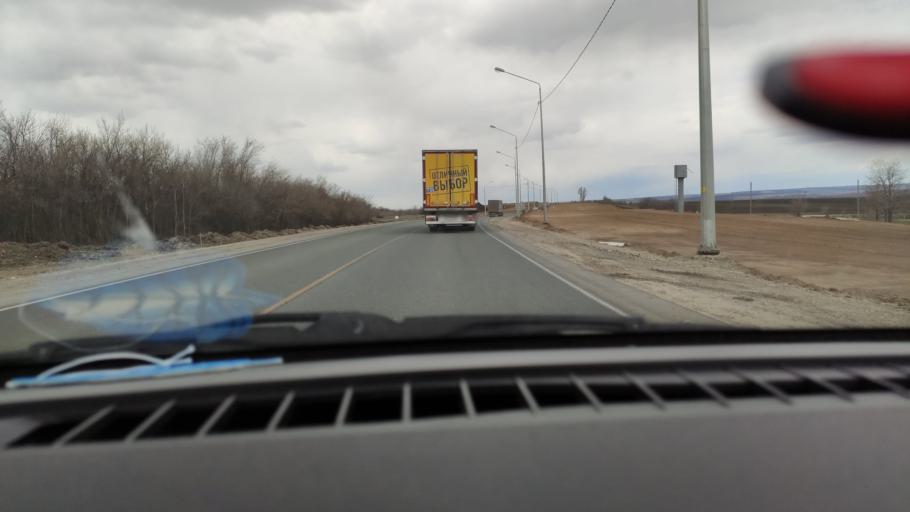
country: RU
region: Saratov
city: Sennoy
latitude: 52.1599
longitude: 47.0576
